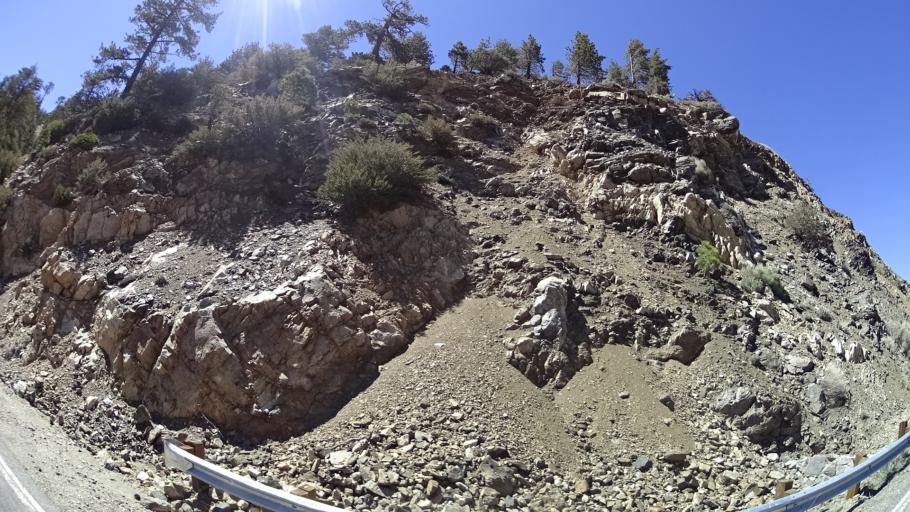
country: US
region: California
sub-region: San Bernardino County
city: Wrightwood
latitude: 34.3664
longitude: -117.8010
